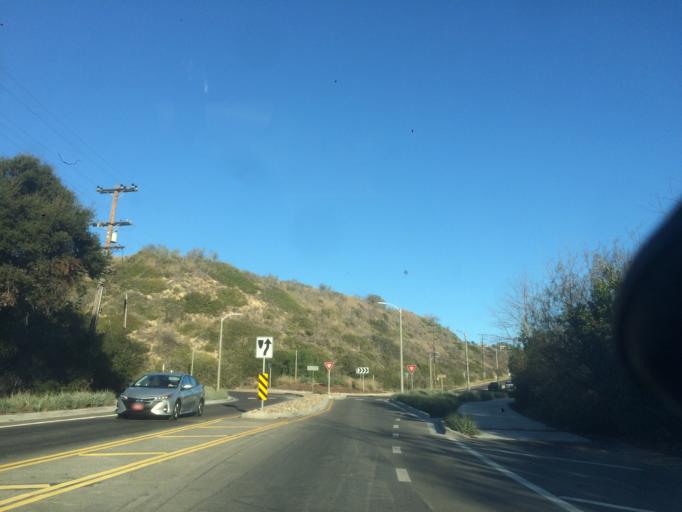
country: US
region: California
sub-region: Santa Barbara County
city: Santa Barbara
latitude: 34.4050
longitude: -119.7401
